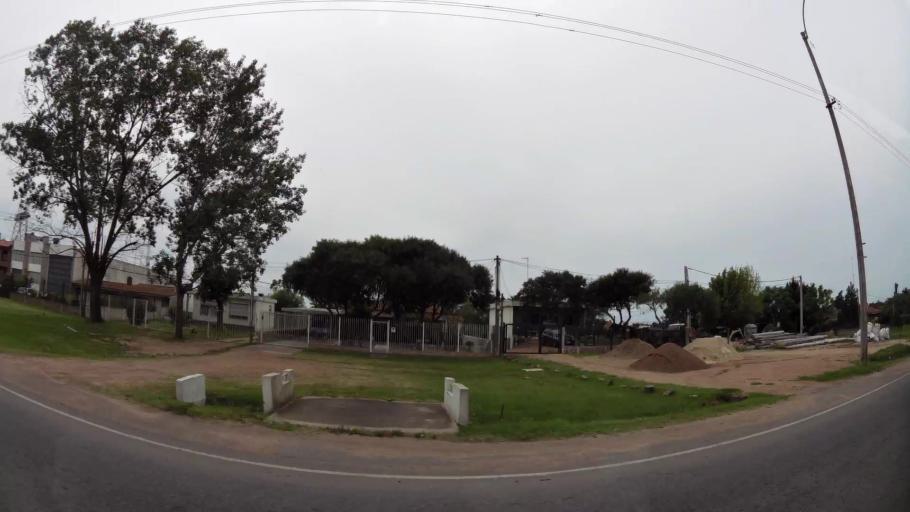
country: UY
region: Canelones
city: La Paz
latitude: -34.7779
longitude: -56.2252
